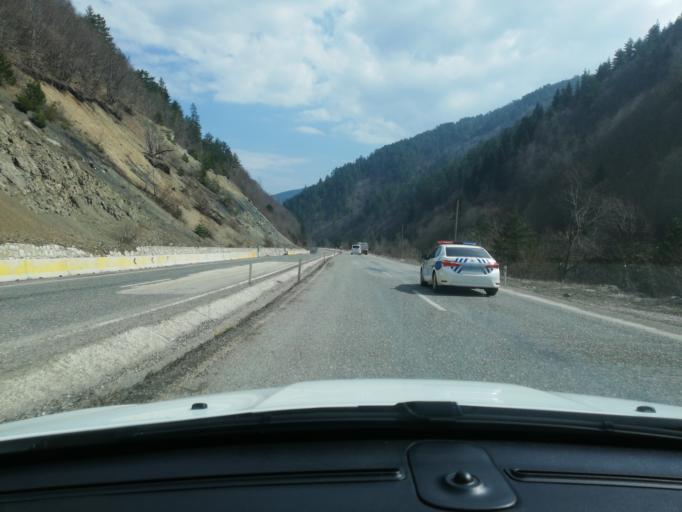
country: TR
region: Kastamonu
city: Kuzyaka
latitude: 41.1218
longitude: 33.7609
